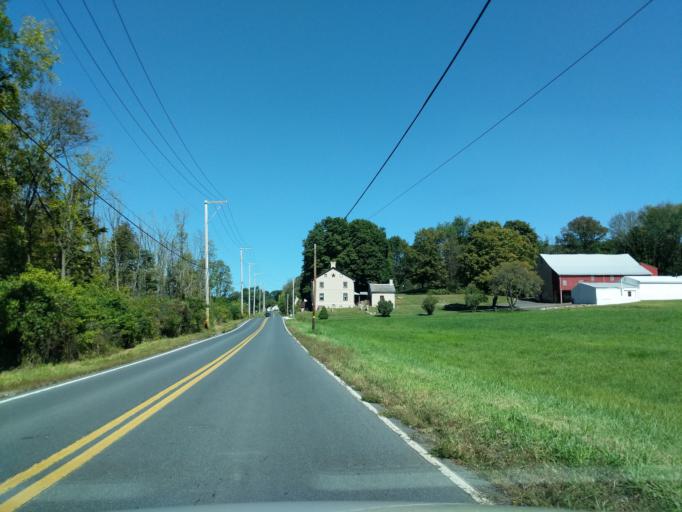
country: US
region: Pennsylvania
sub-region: Bucks County
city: Spinnerstown
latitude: 40.4741
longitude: -75.4669
